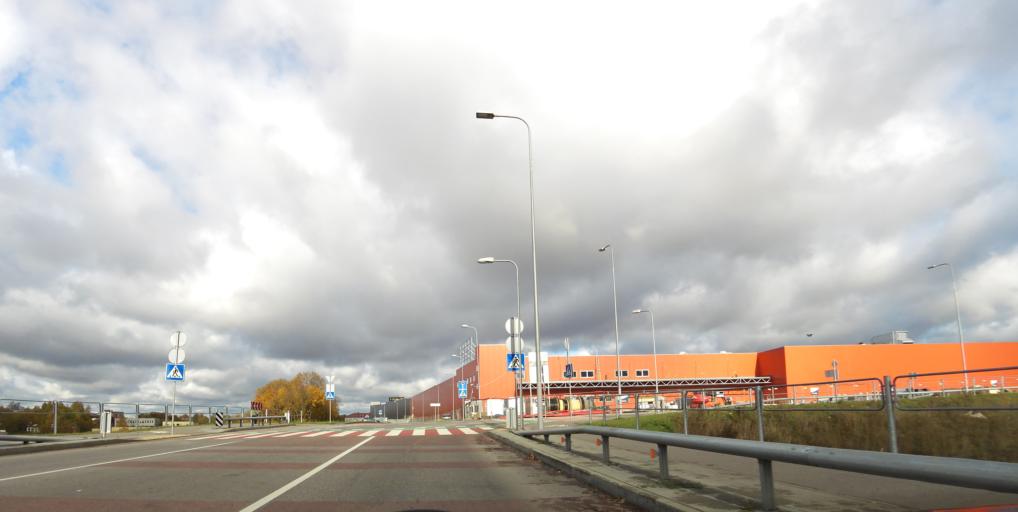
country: LT
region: Vilnius County
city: Naujamiestis
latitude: 54.6497
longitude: 25.2764
